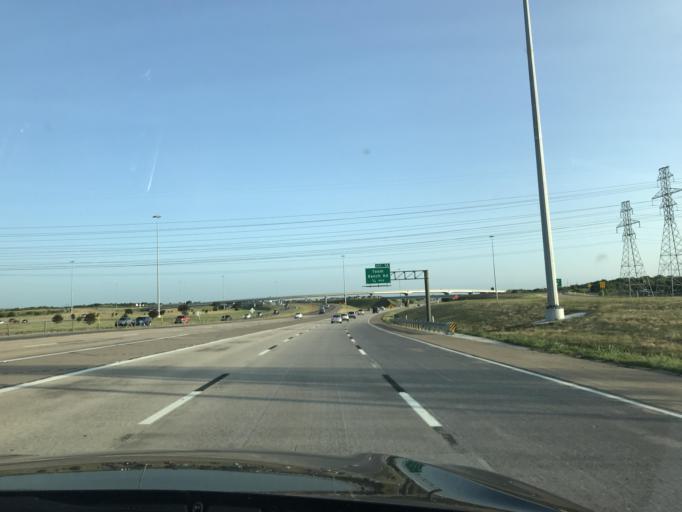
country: US
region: Texas
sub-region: Tarrant County
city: Benbrook
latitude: 32.6883
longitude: -97.4659
